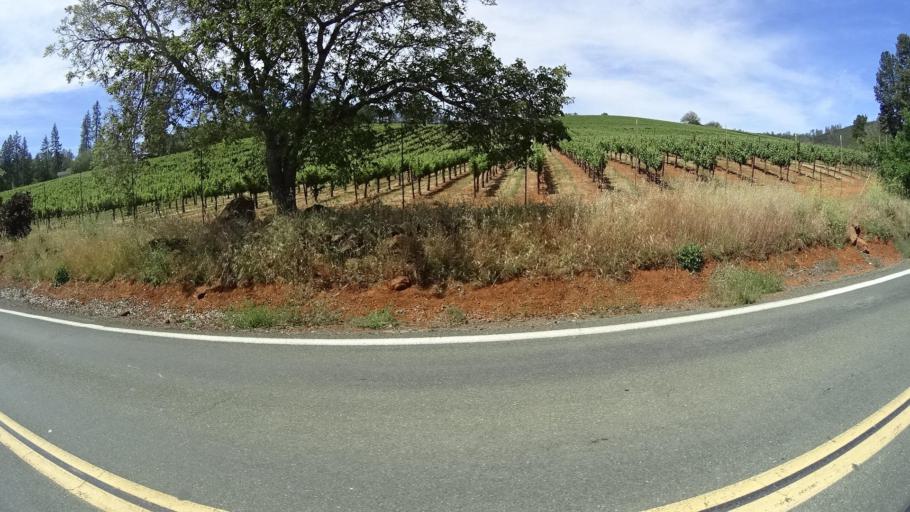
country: US
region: California
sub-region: Lake County
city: Lower Lake
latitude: 38.9134
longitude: -122.6499
